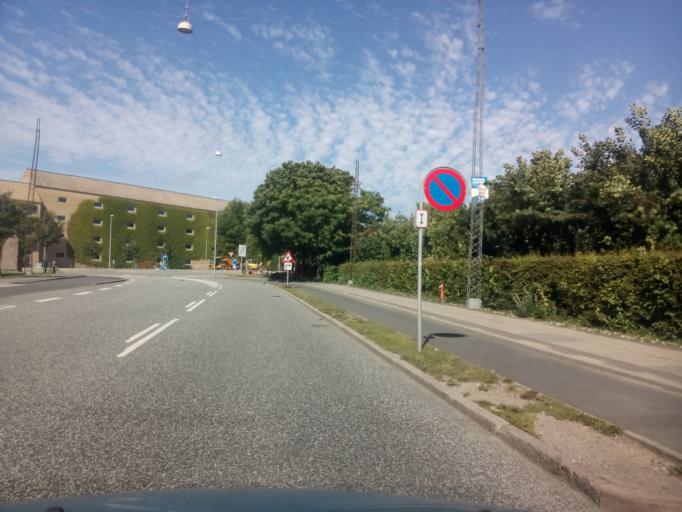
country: DK
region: Central Jutland
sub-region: Arhus Kommune
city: Arhus
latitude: 56.1708
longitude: 10.2067
